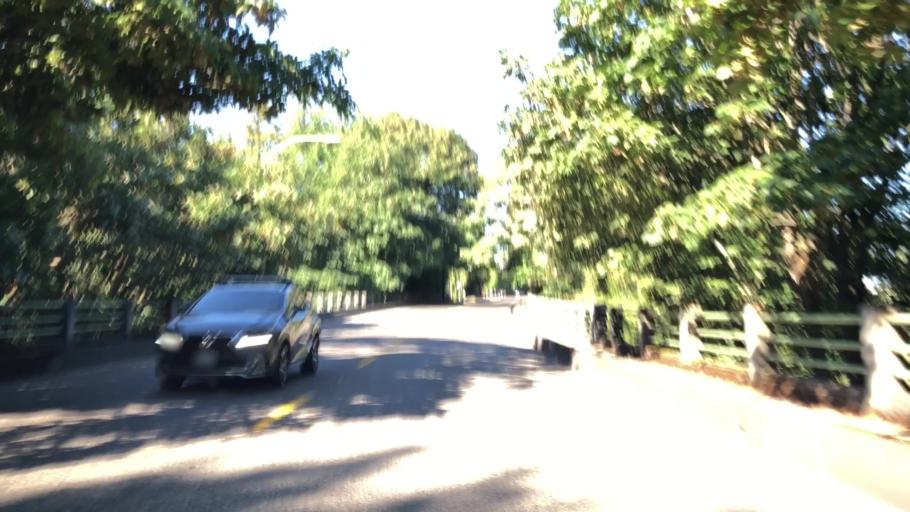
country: US
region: Washington
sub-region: King County
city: Seattle
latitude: 47.6424
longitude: -122.3516
